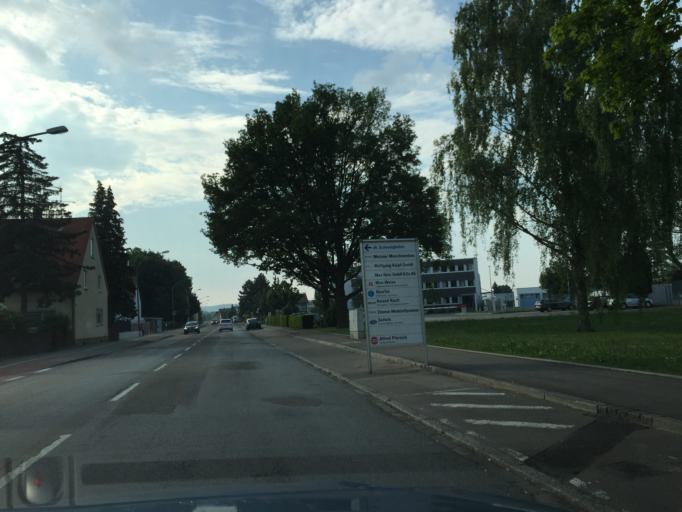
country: DE
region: Bavaria
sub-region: Swabia
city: Neu-Ulm
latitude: 48.3817
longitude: 10.0259
